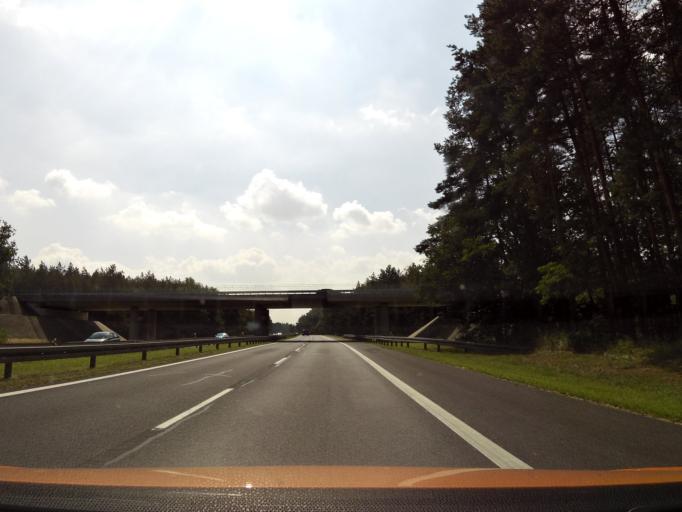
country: PL
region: West Pomeranian Voivodeship
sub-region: Powiat goleniowski
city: Goleniow
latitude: 53.5565
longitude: 14.7959
